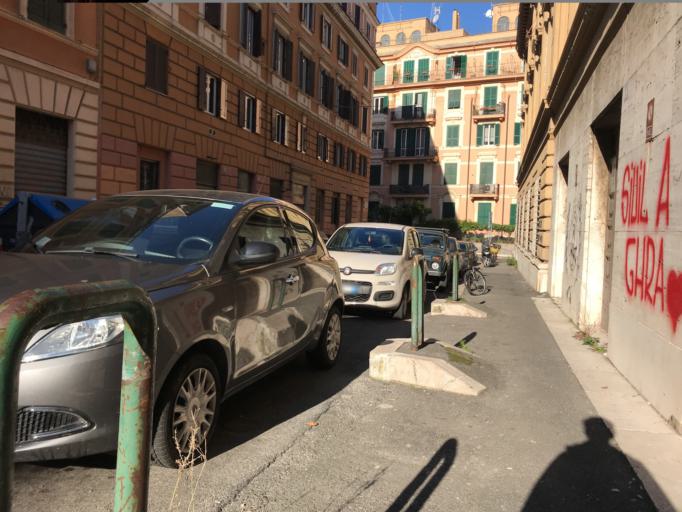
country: IT
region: Latium
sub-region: Citta metropolitana di Roma Capitale
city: Rome
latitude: 41.9127
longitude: 12.5023
